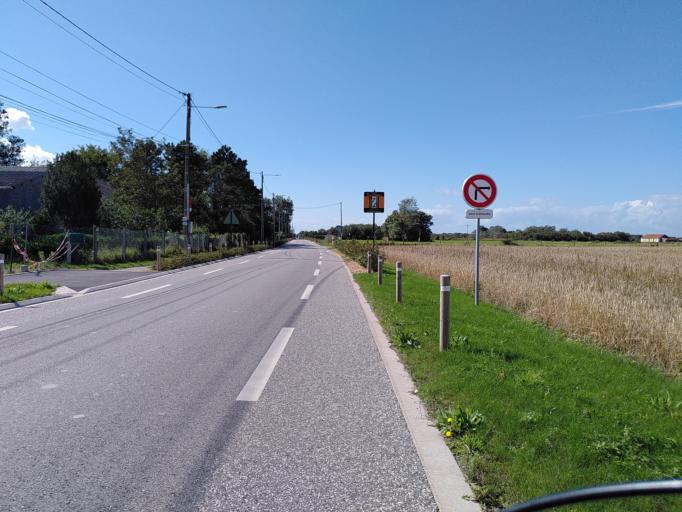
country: FR
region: Nord-Pas-de-Calais
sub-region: Departement du Pas-de-Calais
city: Oye-Plage
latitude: 50.9871
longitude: 2.0563
